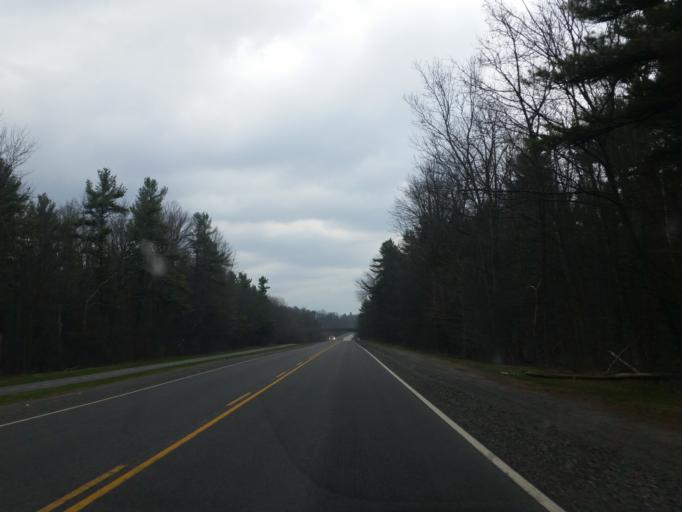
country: CA
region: Ontario
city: Brockville
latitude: 44.4984
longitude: -75.8101
